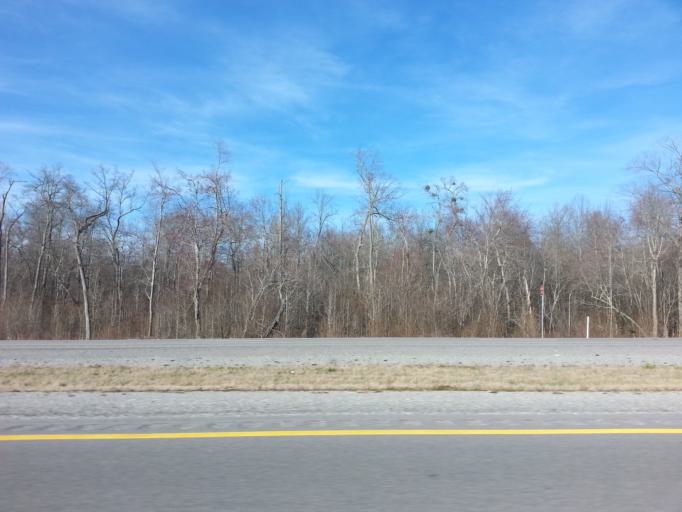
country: US
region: Tennessee
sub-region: Warren County
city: McMinnville
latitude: 35.7159
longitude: -85.8600
